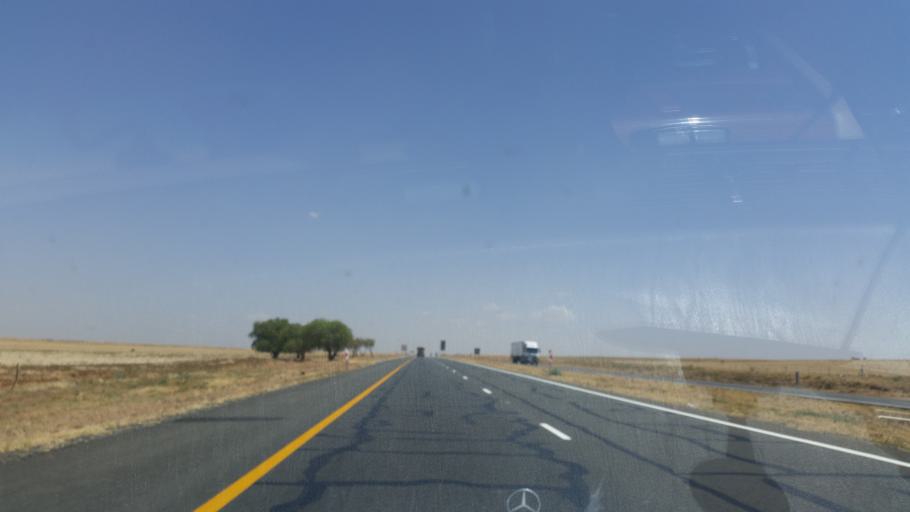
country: ZA
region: Orange Free State
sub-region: Lejweleputswa District Municipality
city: Brandfort
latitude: -28.8682
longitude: 26.5280
